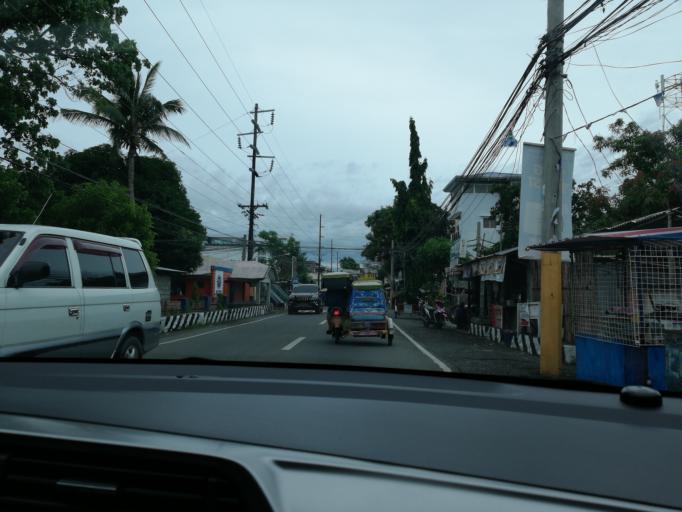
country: PH
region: Ilocos
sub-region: Province of Ilocos Sur
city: Vigan
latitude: 17.5791
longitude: 120.3864
